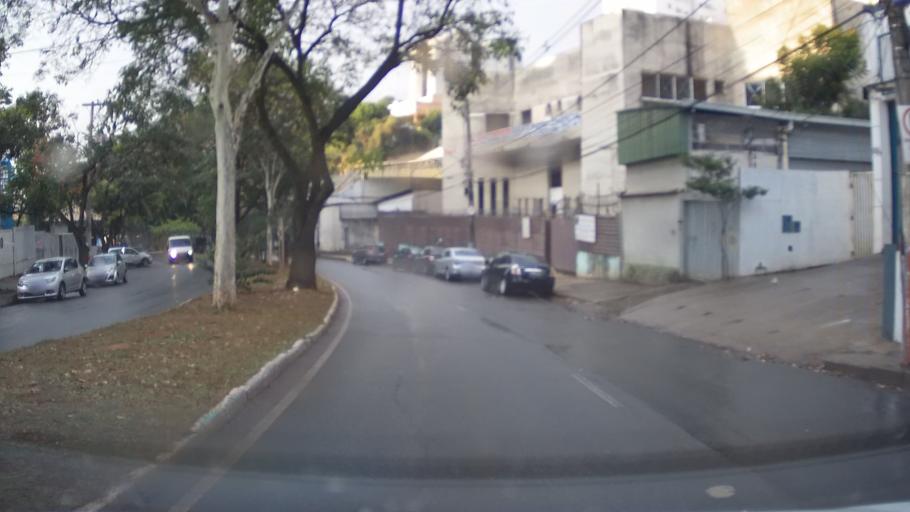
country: BR
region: Minas Gerais
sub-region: Belo Horizonte
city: Belo Horizonte
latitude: -19.9629
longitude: -43.9819
